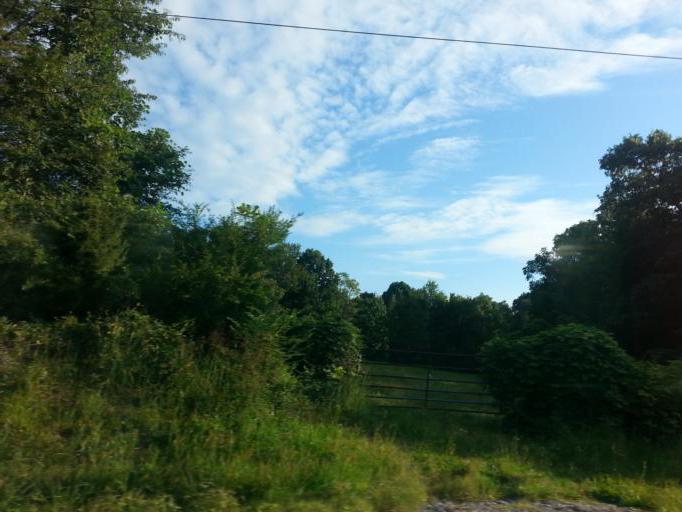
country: US
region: Alabama
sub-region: Lauderdale County
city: Rogersville
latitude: 34.8519
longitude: -87.4027
